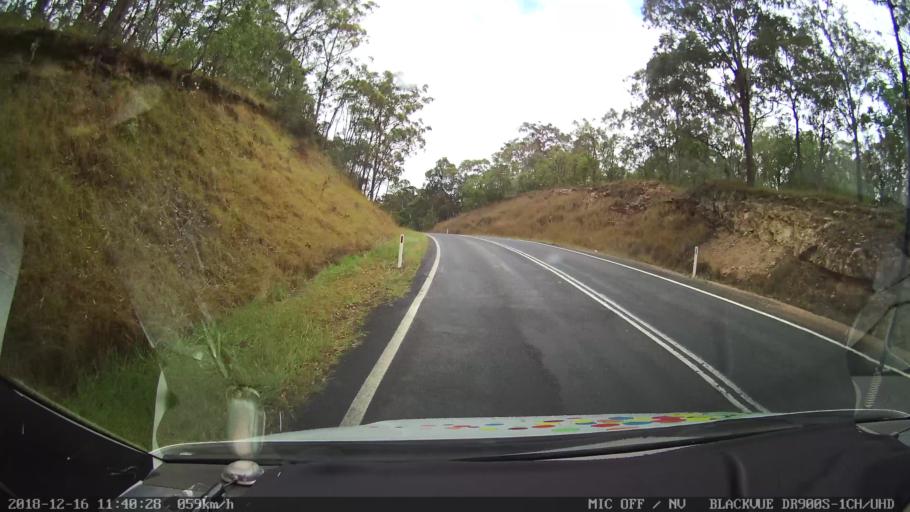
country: AU
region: New South Wales
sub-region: Tenterfield Municipality
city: Carrolls Creek
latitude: -28.9611
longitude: 152.1992
